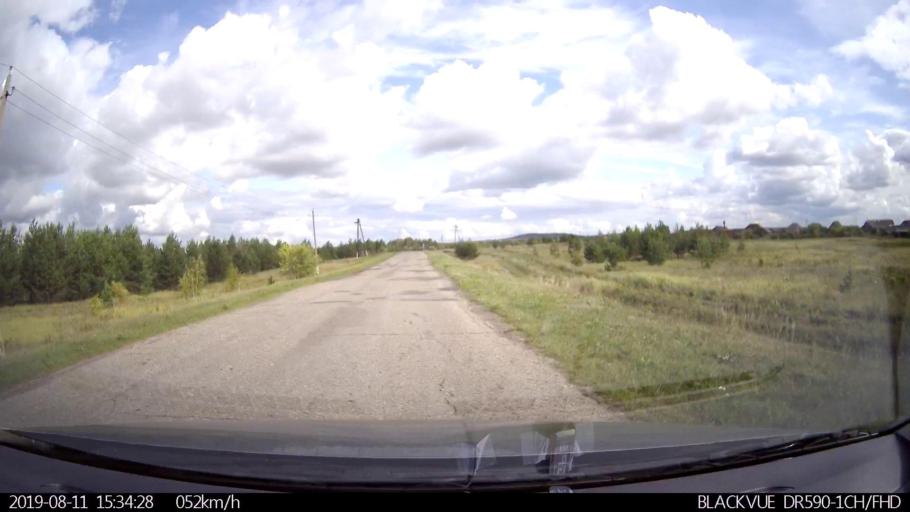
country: RU
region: Ulyanovsk
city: Ignatovka
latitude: 53.8614
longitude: 47.5955
